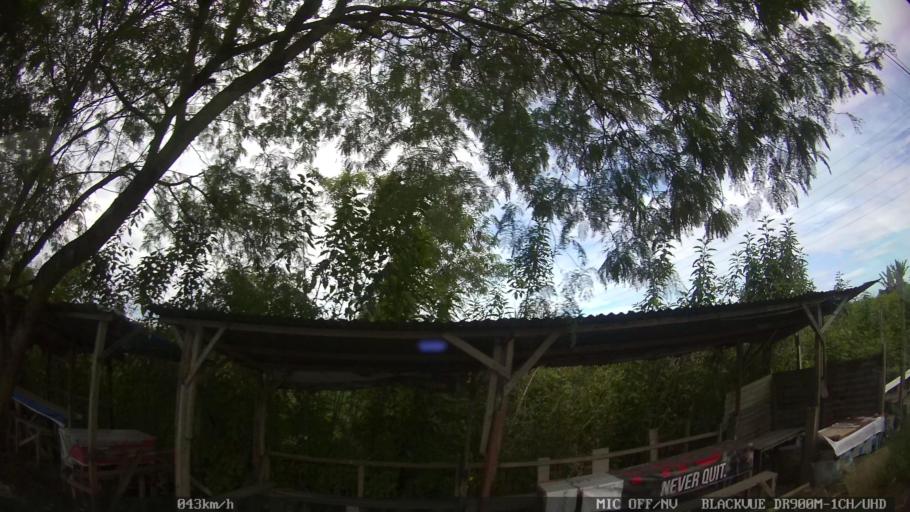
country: ID
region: North Sumatra
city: Sunggal
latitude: 3.5842
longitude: 98.5652
